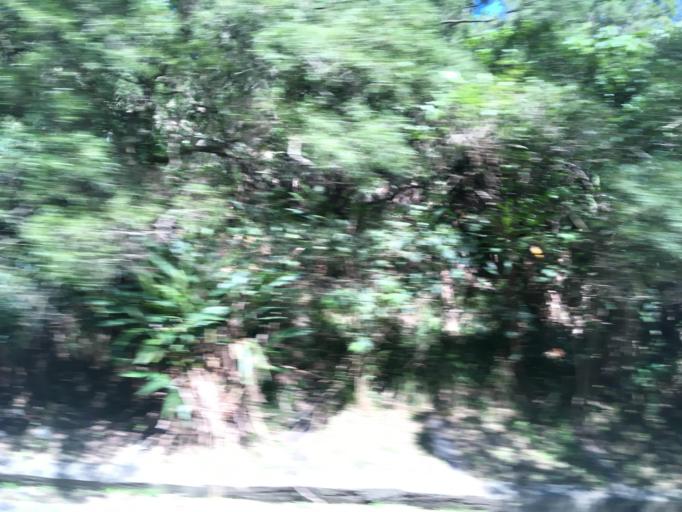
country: TW
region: Taipei
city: Taipei
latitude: 25.0069
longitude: 121.5798
